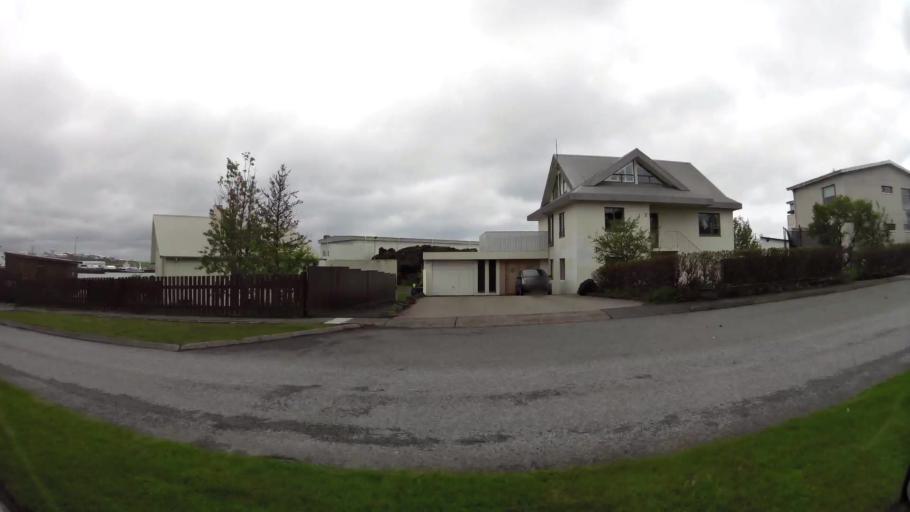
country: IS
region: Capital Region
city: Hafnarfjoerdur
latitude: 64.0728
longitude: -21.9666
